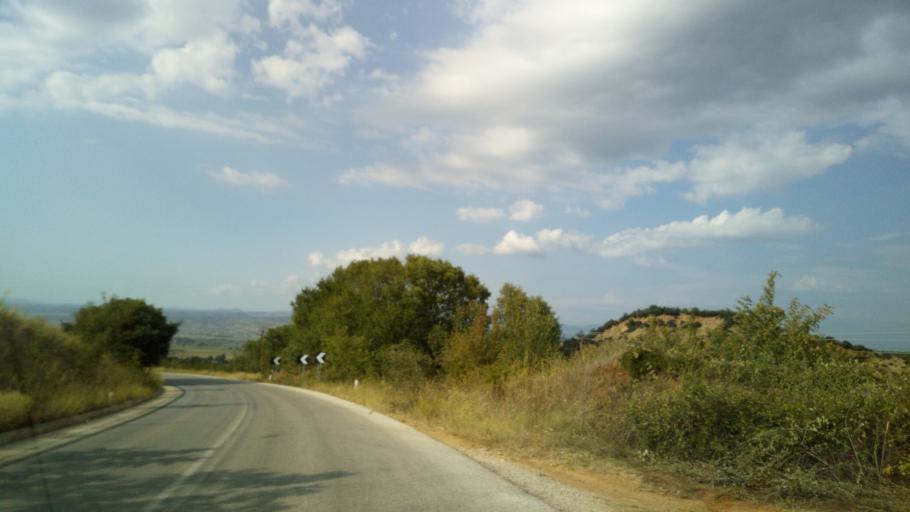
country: GR
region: Central Macedonia
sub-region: Nomos Thessalonikis
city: Gerakarou
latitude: 40.6162
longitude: 23.2235
